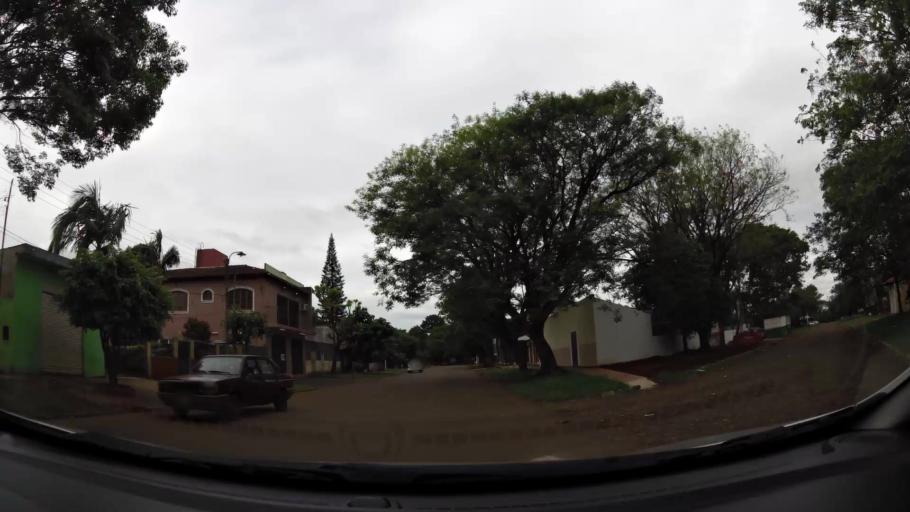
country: PY
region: Alto Parana
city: Ciudad del Este
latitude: -25.4082
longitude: -54.6353
